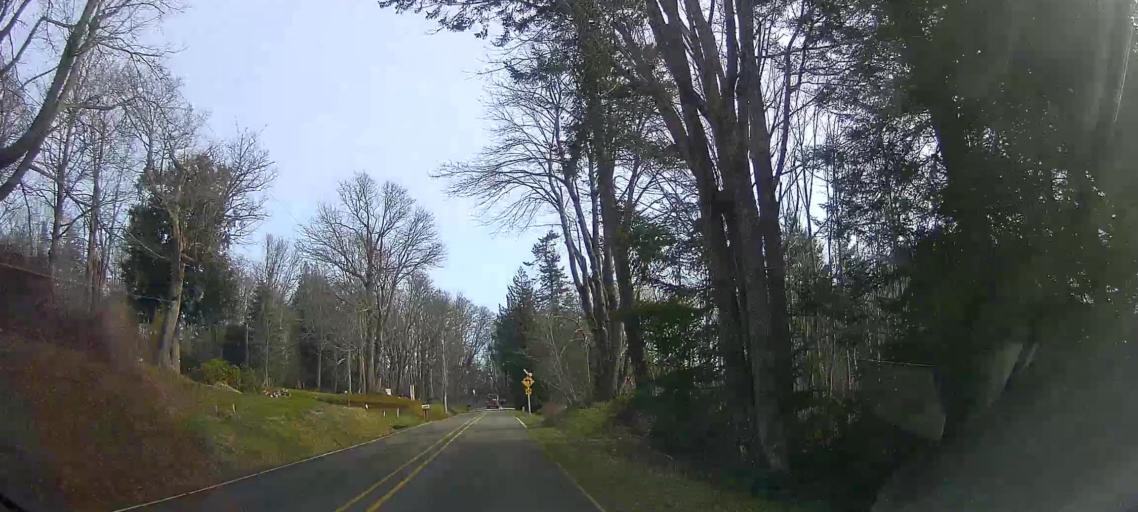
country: US
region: Washington
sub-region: Island County
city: Langley
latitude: 48.0572
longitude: -122.3646
